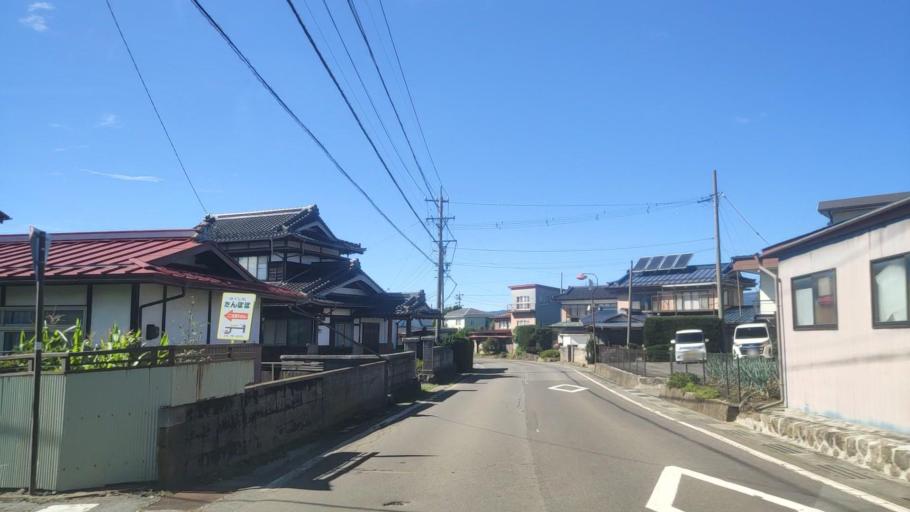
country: JP
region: Nagano
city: Chino
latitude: 35.9817
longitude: 138.2185
